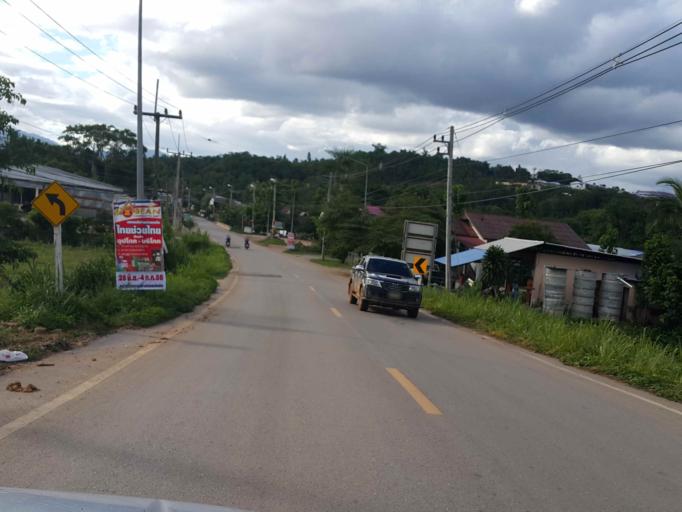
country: TH
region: Chiang Mai
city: Mae Chaem
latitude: 18.4898
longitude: 98.3776
